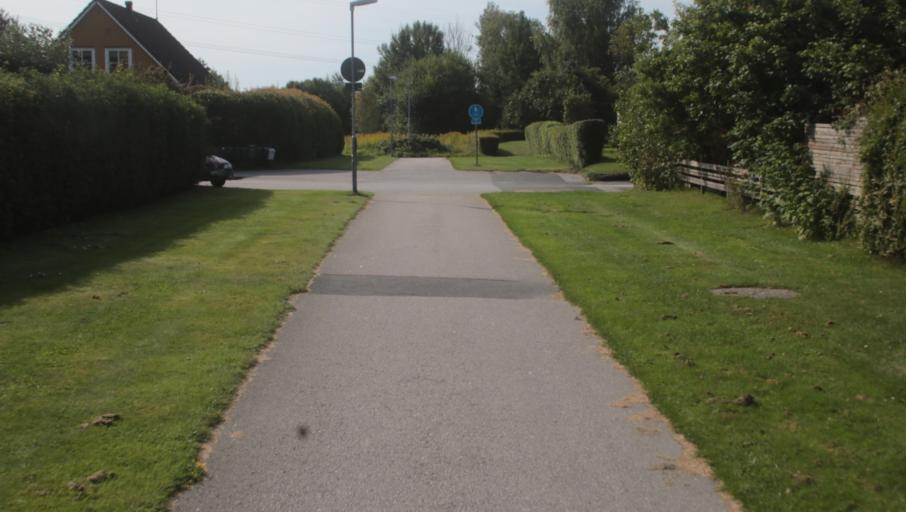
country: SE
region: Blekinge
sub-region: Karlshamns Kommun
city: Karlshamn
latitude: 56.1975
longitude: 14.8451
